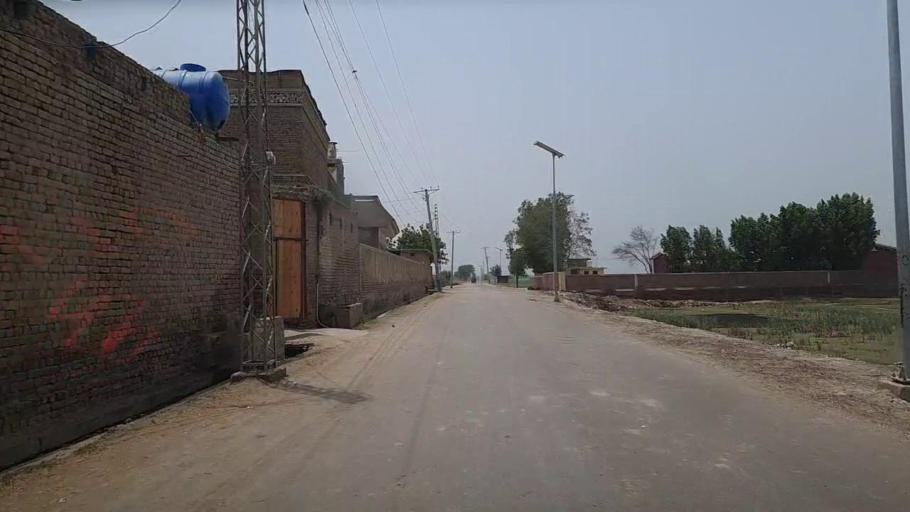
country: PK
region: Sindh
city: Sita Road
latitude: 27.0591
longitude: 67.9037
